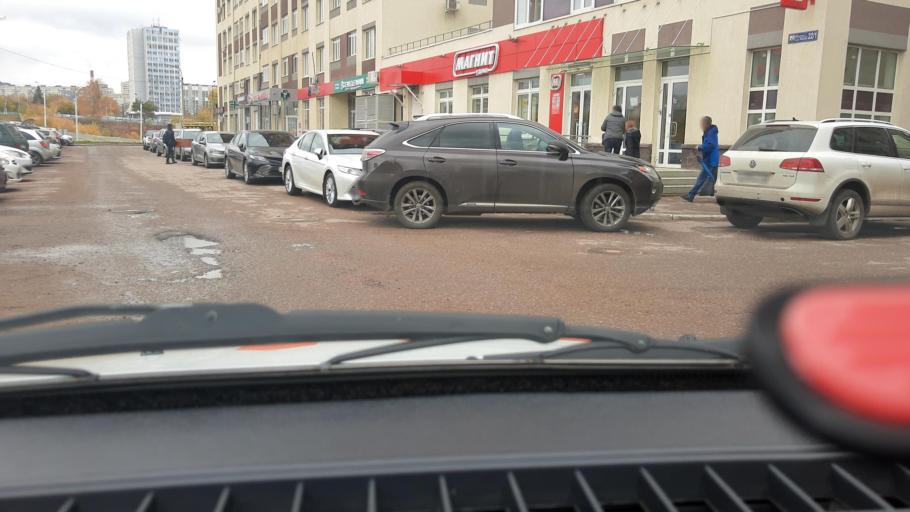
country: RU
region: Bashkortostan
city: Ufa
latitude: 54.7173
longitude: 55.9797
